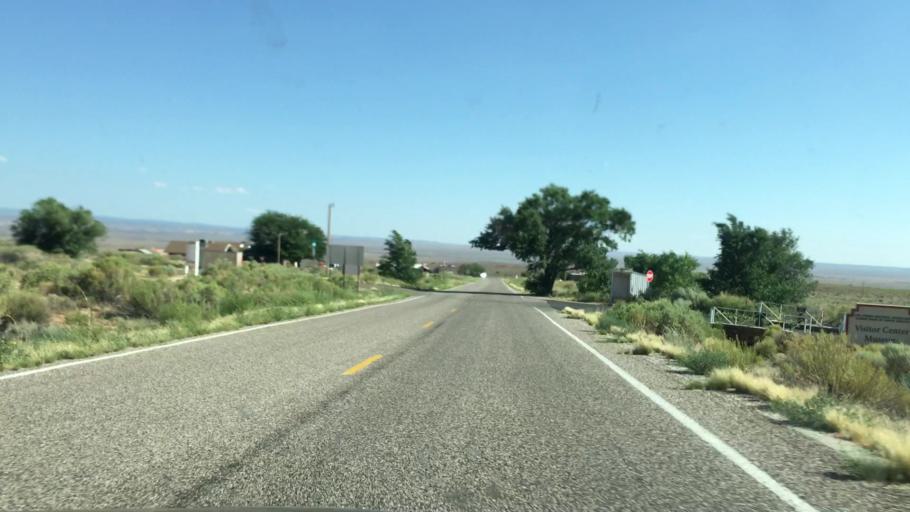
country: US
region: Arizona
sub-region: Coconino County
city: Fredonia
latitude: 36.8625
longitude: -112.7367
